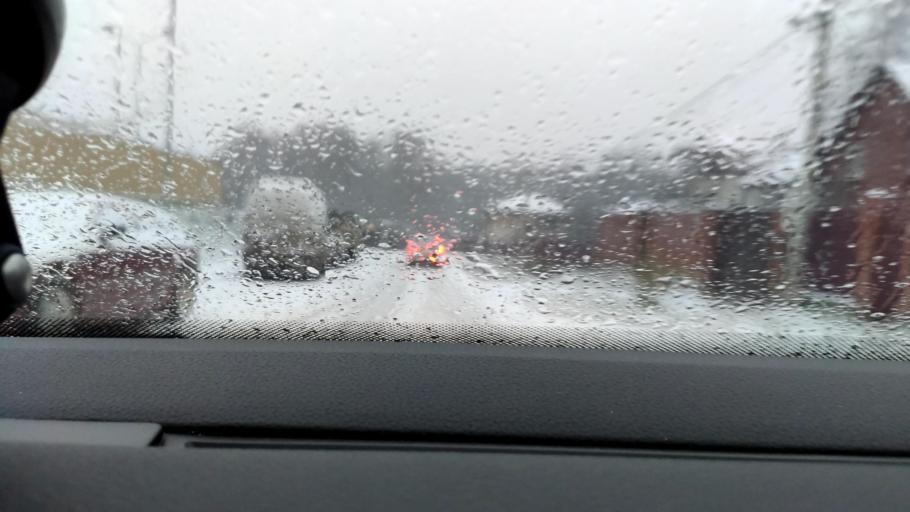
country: RU
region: Moscow
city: Zyablikovo
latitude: 55.5981
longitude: 37.7628
